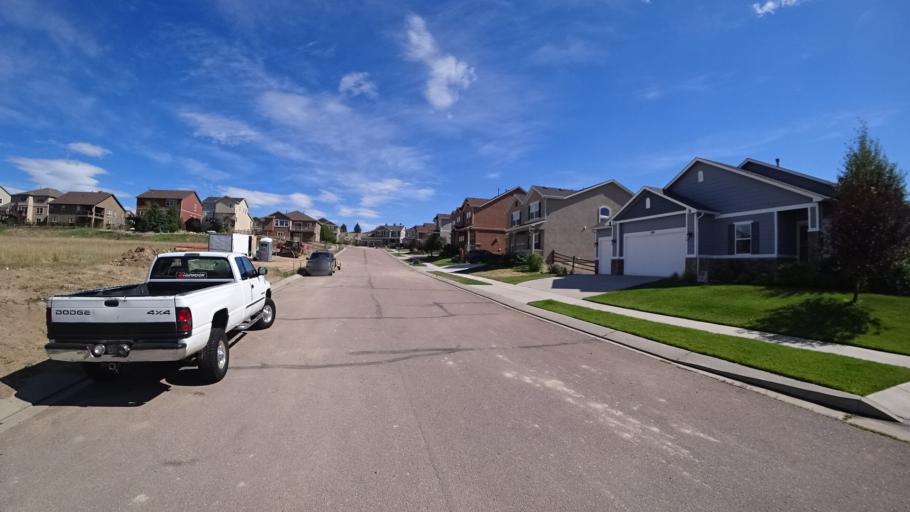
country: US
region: Colorado
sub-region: El Paso County
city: Gleneagle
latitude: 39.0255
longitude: -104.8086
